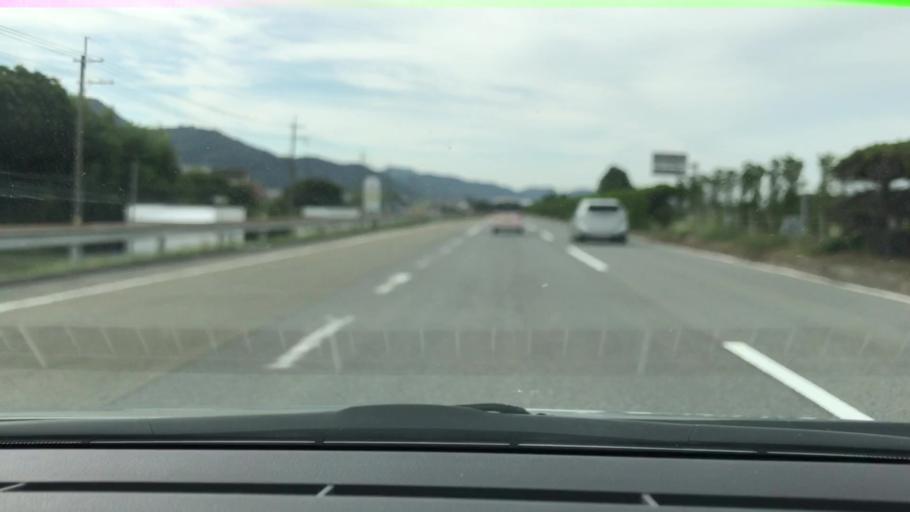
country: JP
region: Hyogo
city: Himeji
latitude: 34.9096
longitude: 134.7541
